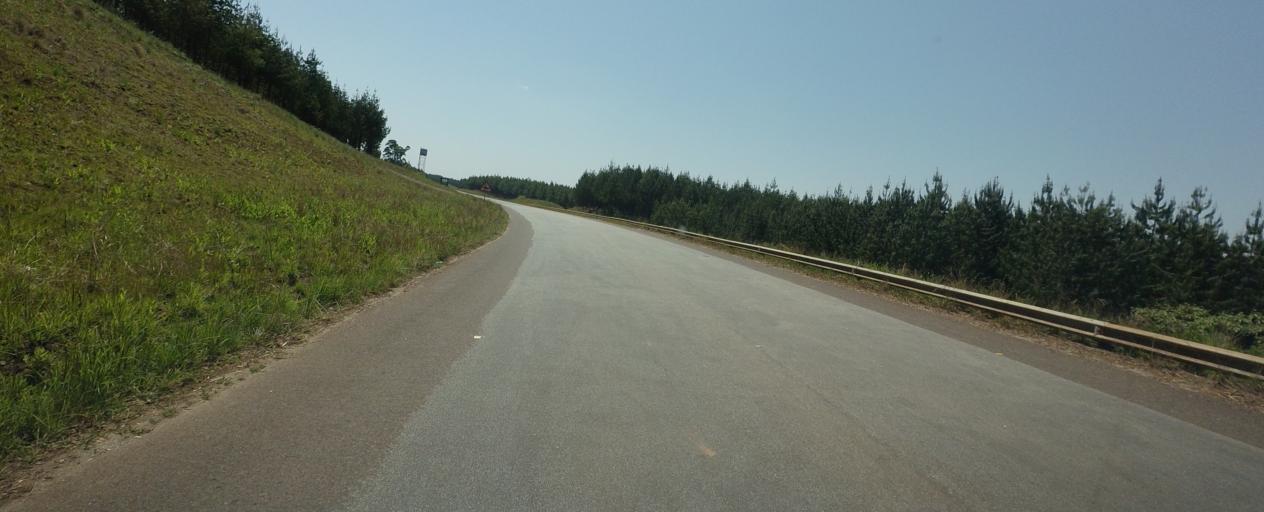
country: ZA
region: Mpumalanga
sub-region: Ehlanzeni District
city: Graksop
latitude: -24.9069
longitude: 30.8450
